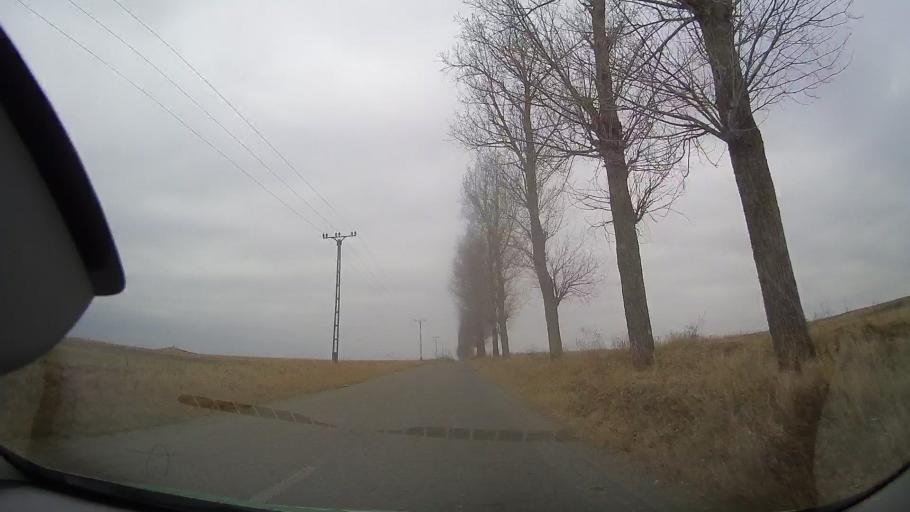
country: RO
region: Buzau
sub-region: Comuna Pogoanele
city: Pogoanele
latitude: 44.9623
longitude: 27.0214
